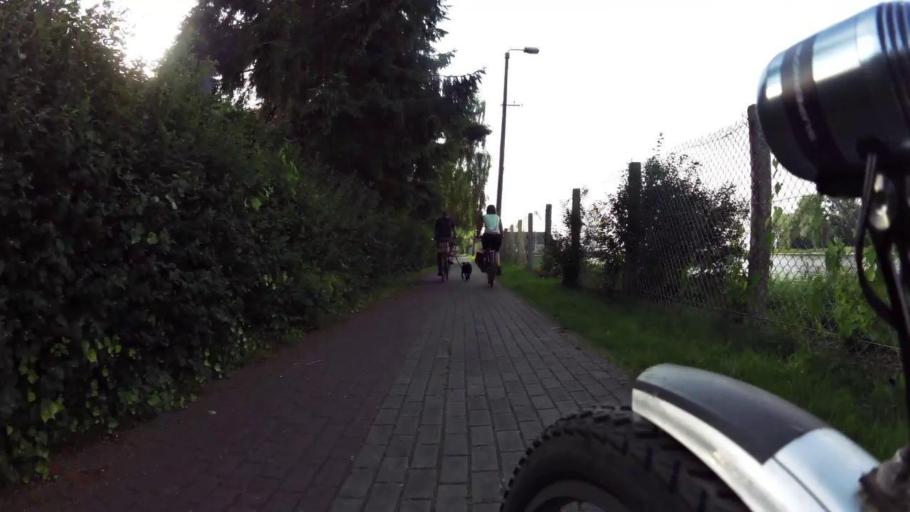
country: PL
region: West Pomeranian Voivodeship
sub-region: Powiat goleniowski
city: Stepnica
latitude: 53.6605
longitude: 14.5165
